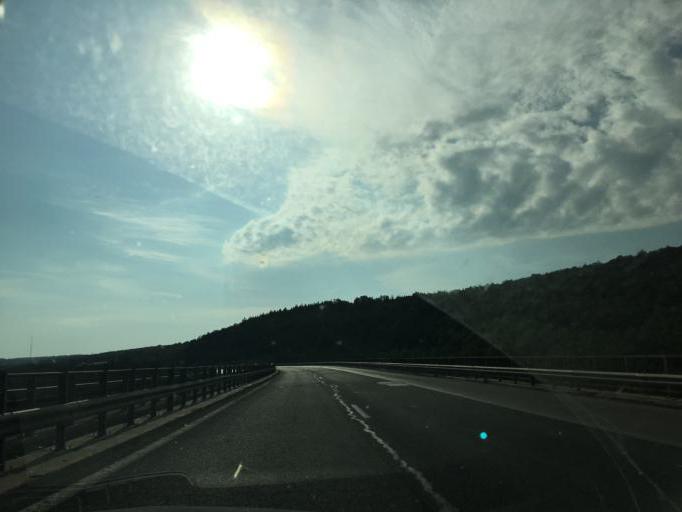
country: BG
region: Sofiya
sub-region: Obshtina Elin Pelin
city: Elin Pelin
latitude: 42.5843
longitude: 23.6386
